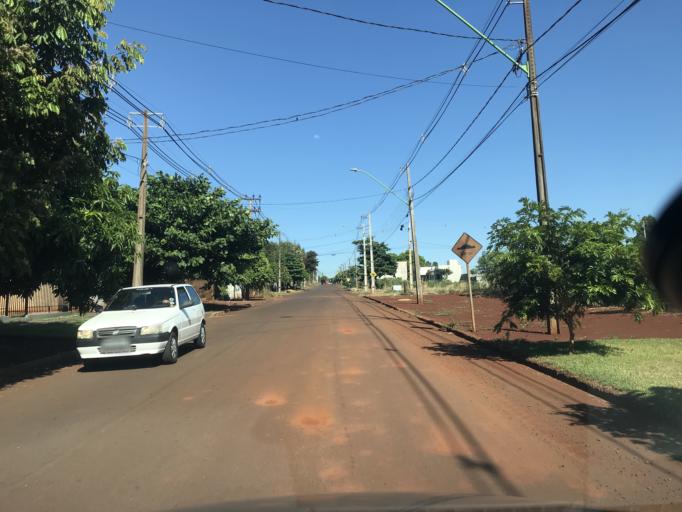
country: BR
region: Parana
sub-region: Palotina
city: Palotina
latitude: -24.2740
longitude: -53.8272
